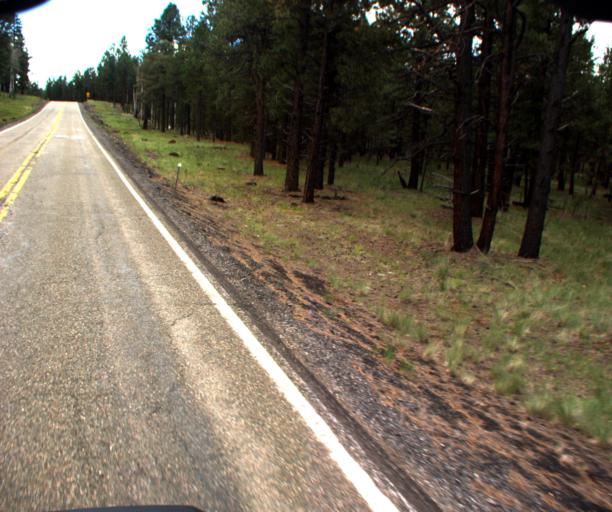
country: US
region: Arizona
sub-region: Coconino County
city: Parks
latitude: 35.3556
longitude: -111.7909
